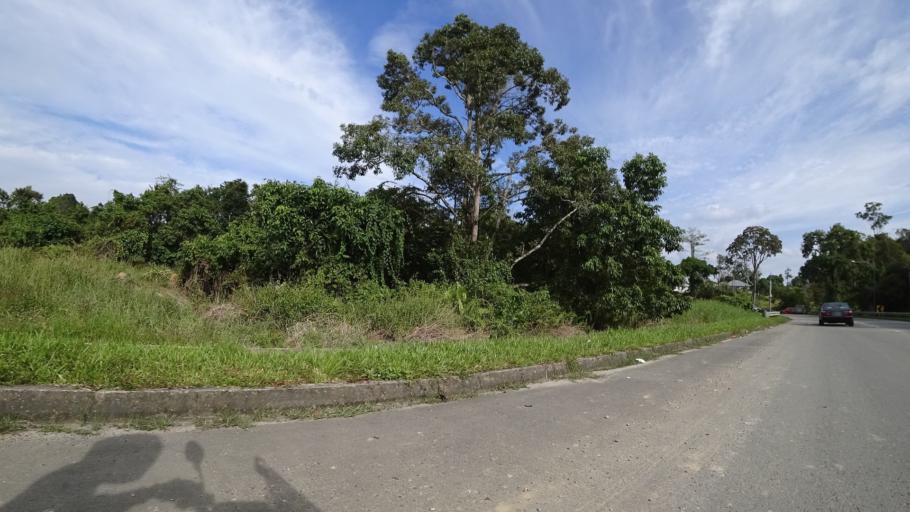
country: BN
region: Brunei and Muara
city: Bandar Seri Begawan
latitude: 4.8703
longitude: 114.8082
